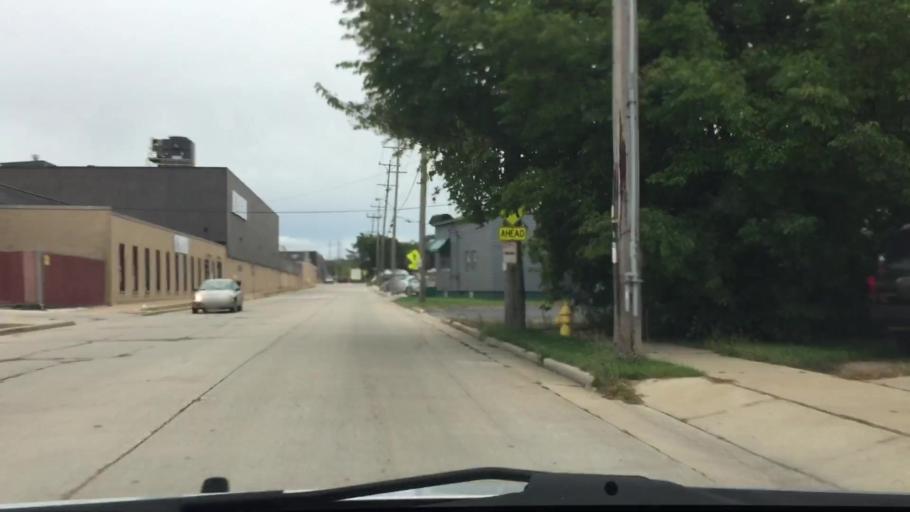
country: US
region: Wisconsin
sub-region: Waukesha County
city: Waukesha
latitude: 43.0192
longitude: -88.2190
